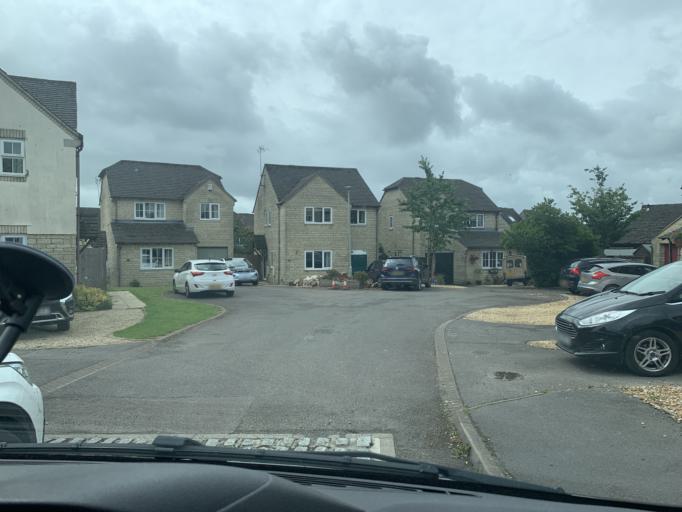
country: GB
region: England
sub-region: Gloucestershire
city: Chalford
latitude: 51.7325
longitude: -2.1603
